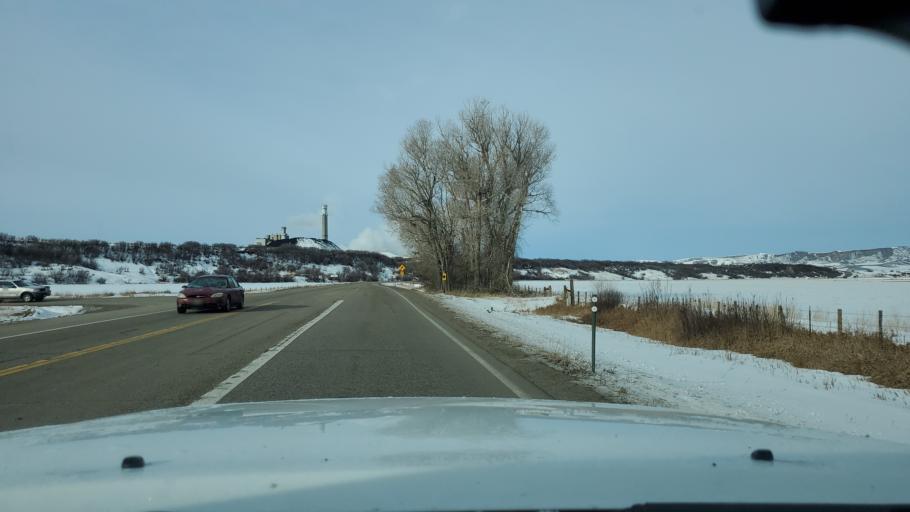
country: US
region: Colorado
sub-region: Routt County
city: Hayden
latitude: 40.4883
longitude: -107.1694
